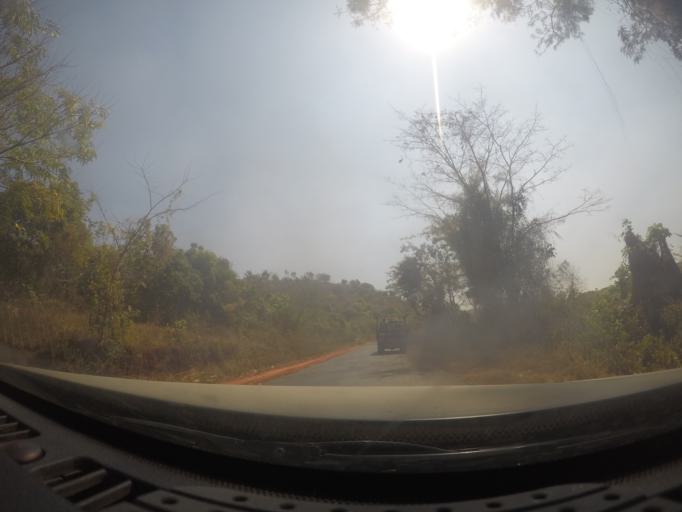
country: MM
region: Shan
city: Taunggyi
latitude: 20.8141
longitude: 97.2266
